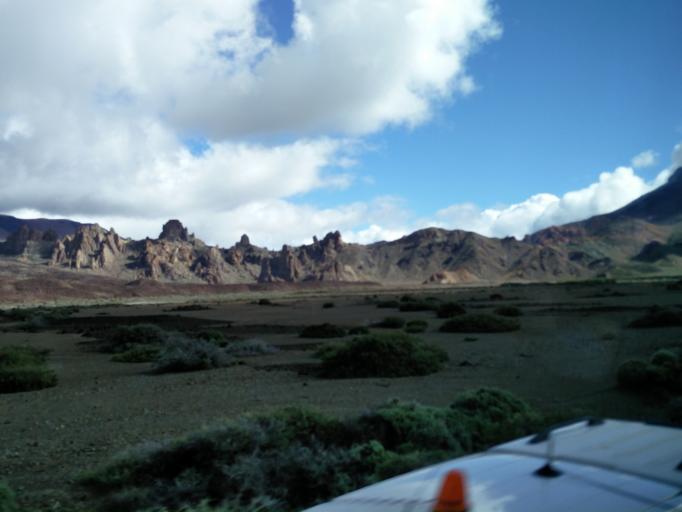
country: ES
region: Canary Islands
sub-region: Provincia de Santa Cruz de Tenerife
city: Vilaflor
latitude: 28.2106
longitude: -16.6496
